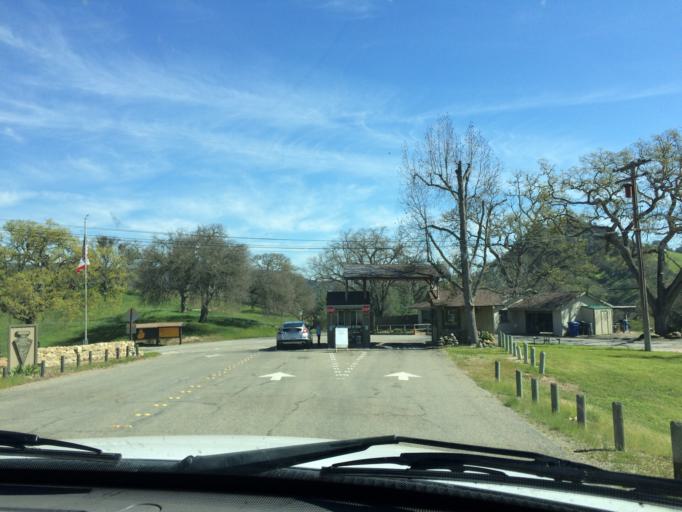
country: US
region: California
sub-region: San Luis Obispo County
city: Santa Margarita
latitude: 35.3247
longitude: -120.4930
